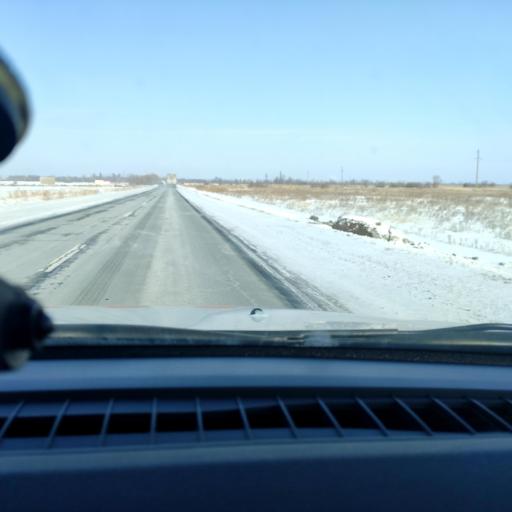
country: RU
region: Samara
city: Smyshlyayevka
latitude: 53.1629
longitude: 50.4570
